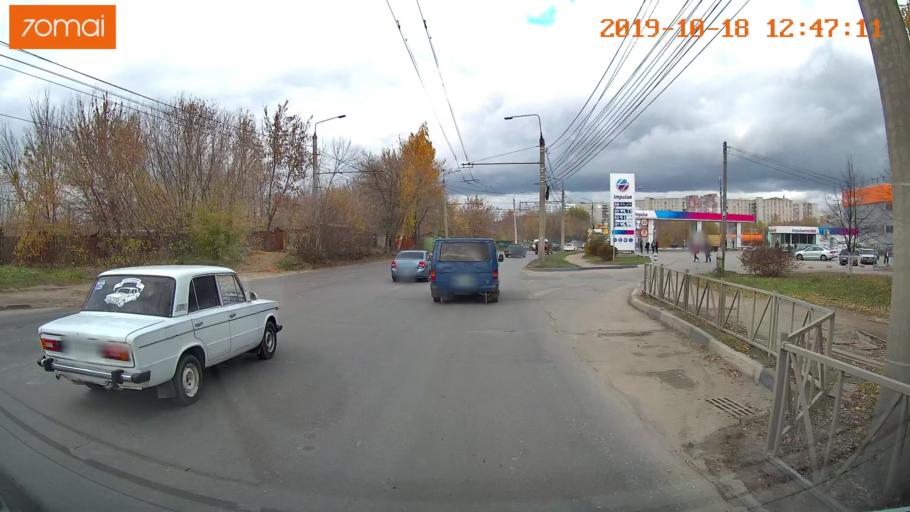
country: RU
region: Rjazan
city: Ryazan'
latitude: 54.6571
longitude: 39.6634
